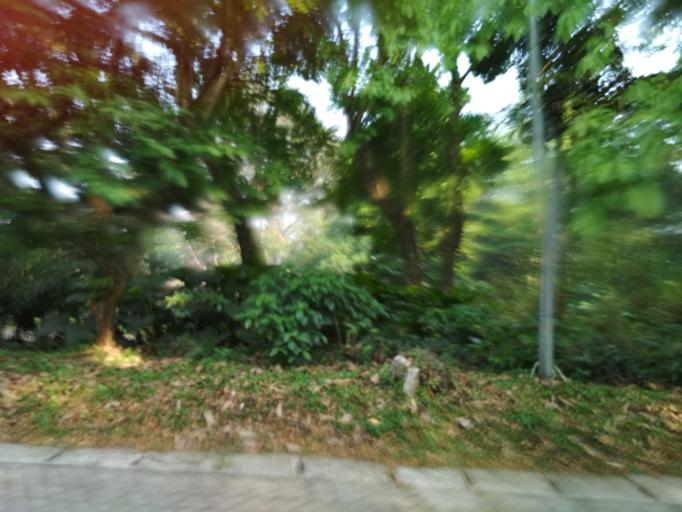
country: ID
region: West Java
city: Ciampea
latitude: -6.5604
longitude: 106.7301
